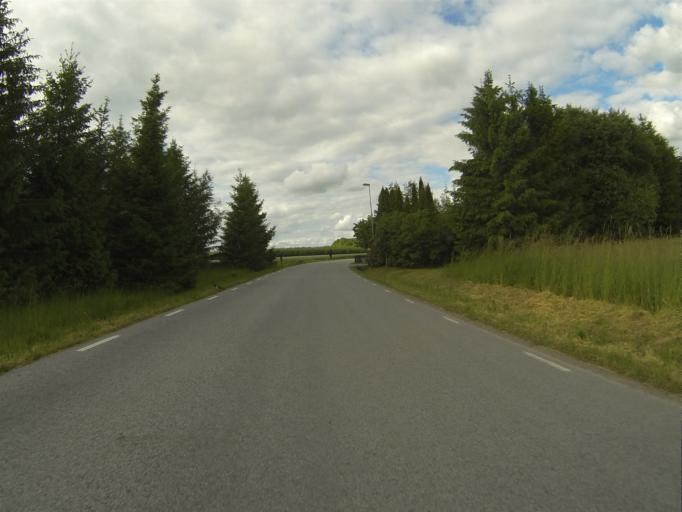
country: SE
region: Skane
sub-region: Staffanstorps Kommun
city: Staffanstorp
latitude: 55.6275
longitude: 13.2202
